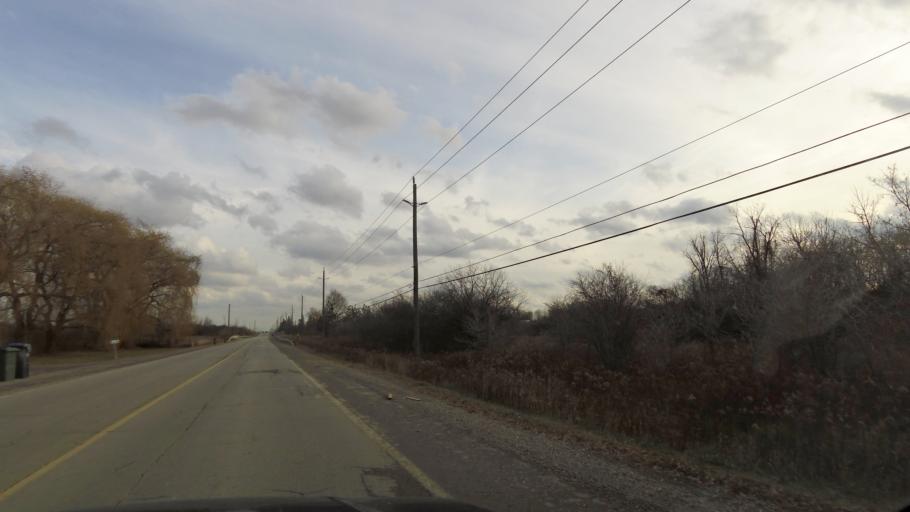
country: CA
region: Ontario
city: Brampton
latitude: 43.7871
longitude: -79.7067
